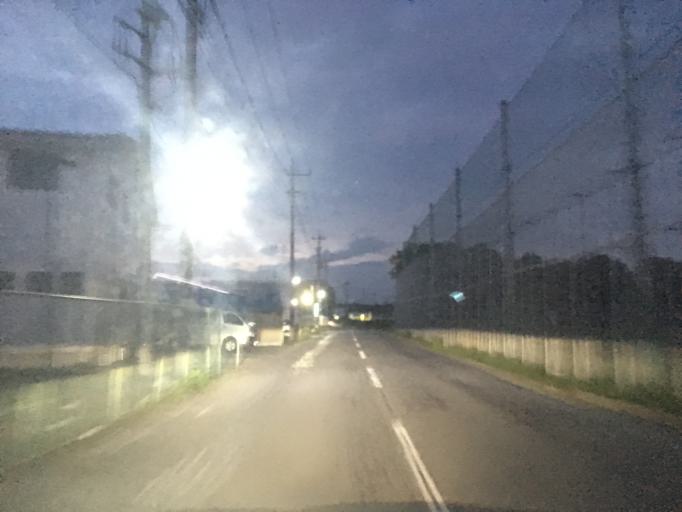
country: JP
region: Saitama
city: Sayama
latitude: 35.8020
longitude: 139.3887
